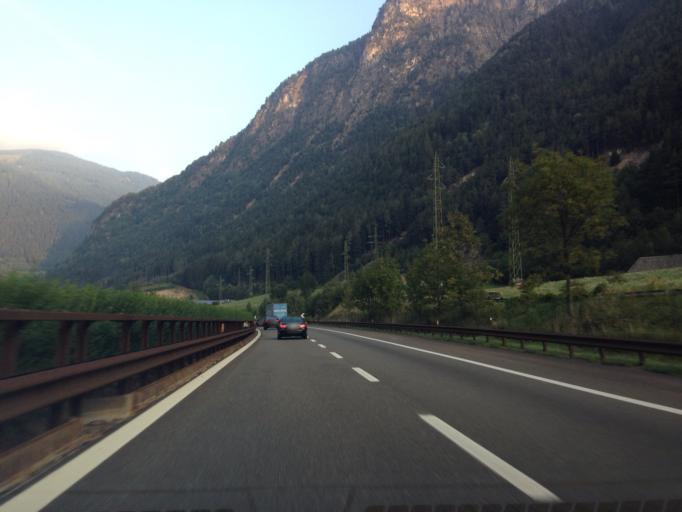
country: IT
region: Trentino-Alto Adige
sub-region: Bolzano
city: Fortezza
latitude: 46.8105
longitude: 11.5618
